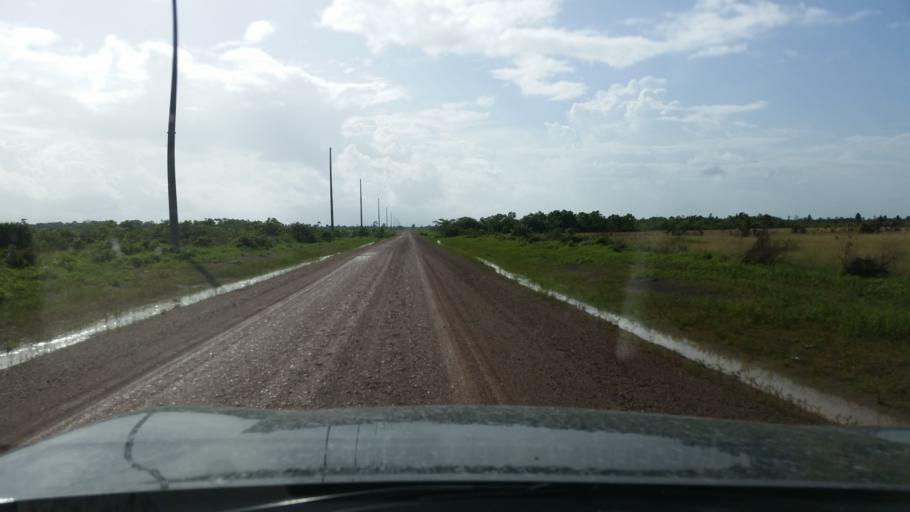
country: NI
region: Atlantico Norte (RAAN)
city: Puerto Cabezas
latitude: 14.1092
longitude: -83.5861
